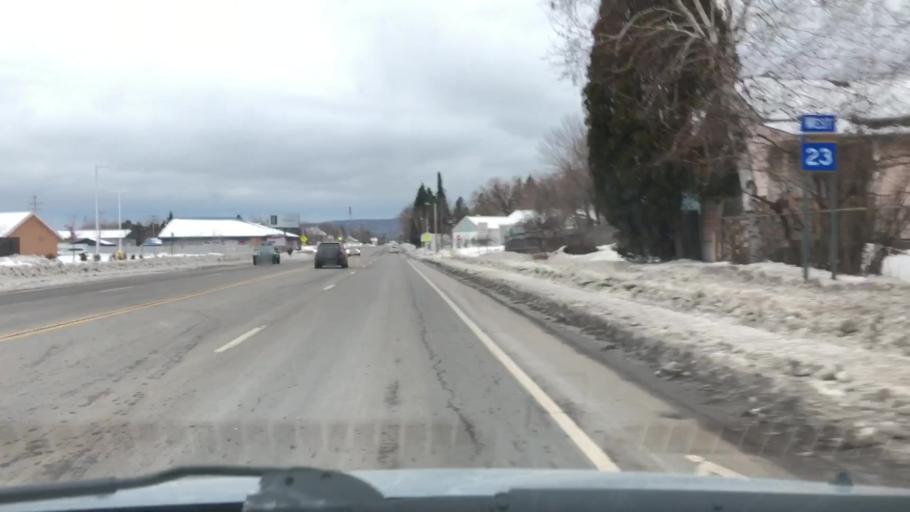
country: US
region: Minnesota
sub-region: Saint Louis County
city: Proctor
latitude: 46.7311
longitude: -92.1803
